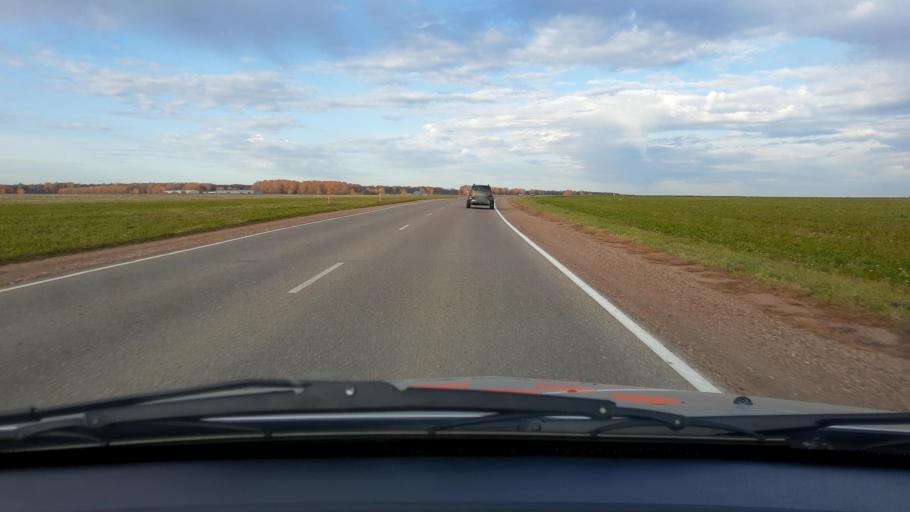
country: RU
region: Bashkortostan
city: Avdon
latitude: 54.8216
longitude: 55.6699
